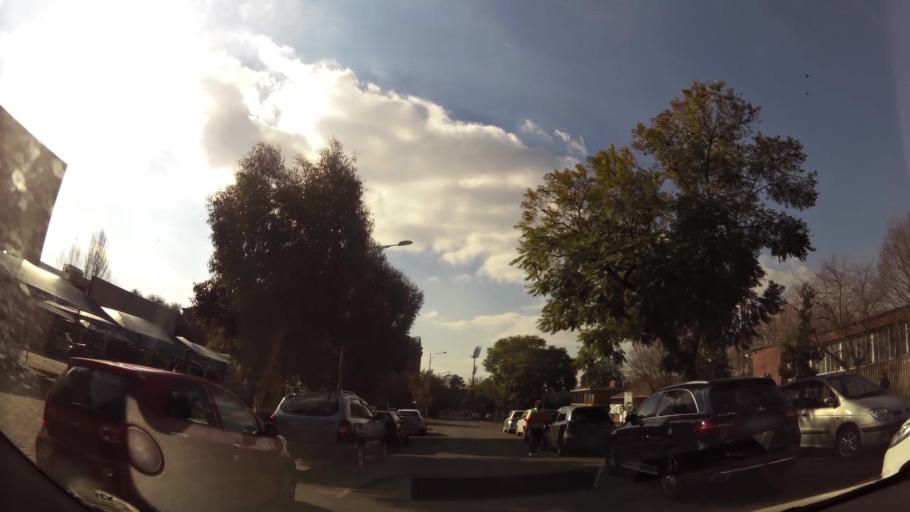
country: ZA
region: Gauteng
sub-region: West Rand District Municipality
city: Krugersdorp
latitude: -26.1050
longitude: 27.7760
